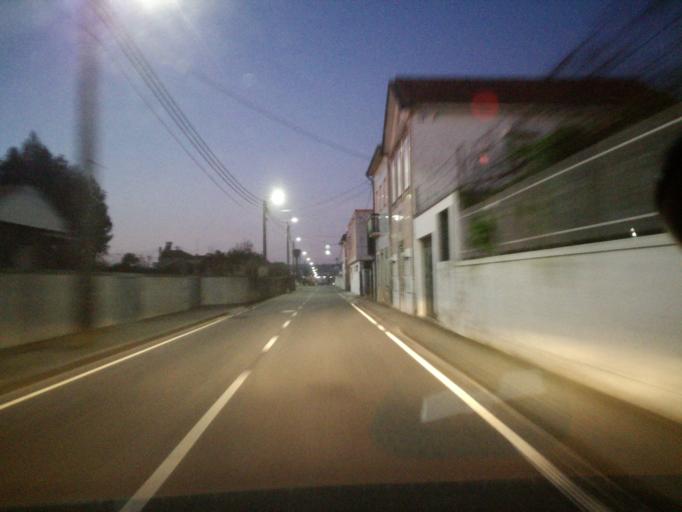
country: PT
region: Porto
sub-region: Maia
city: Nogueira
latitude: 41.2428
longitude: -8.5865
